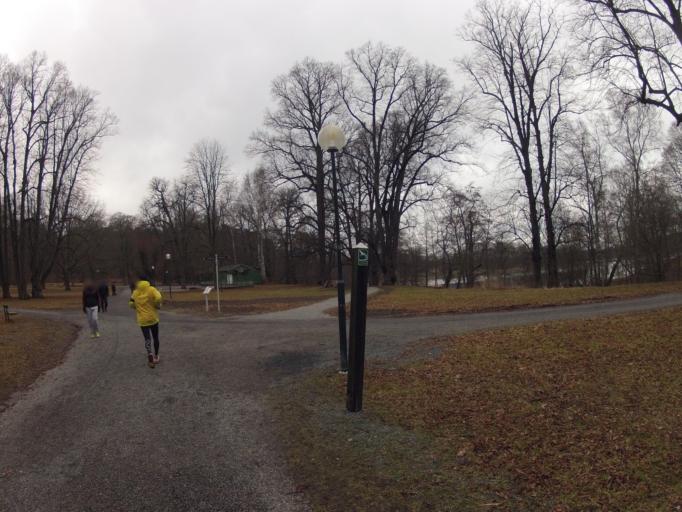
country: SE
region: Stockholm
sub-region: Norrtalje Kommun
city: Bergshamra
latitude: 59.3582
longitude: 18.0413
